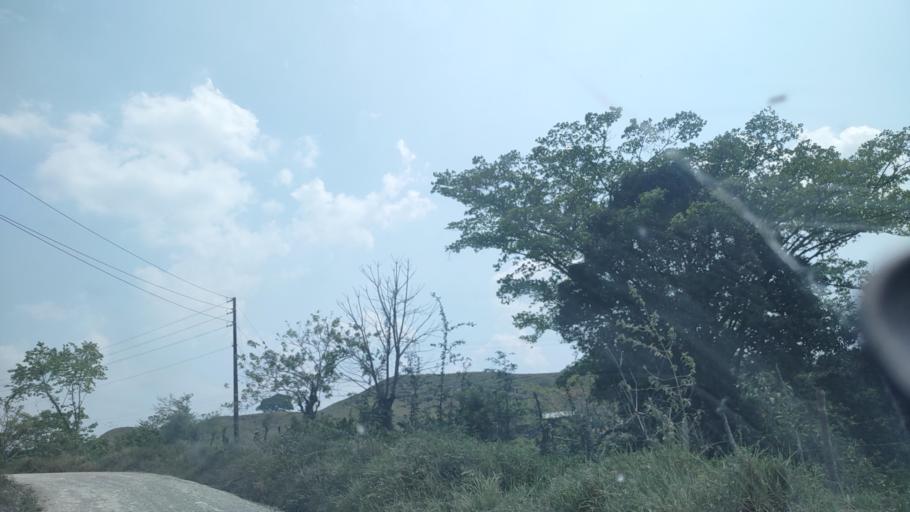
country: MX
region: Tabasco
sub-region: Huimanguillo
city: Francisco Rueda
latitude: 17.6044
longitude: -93.9058
